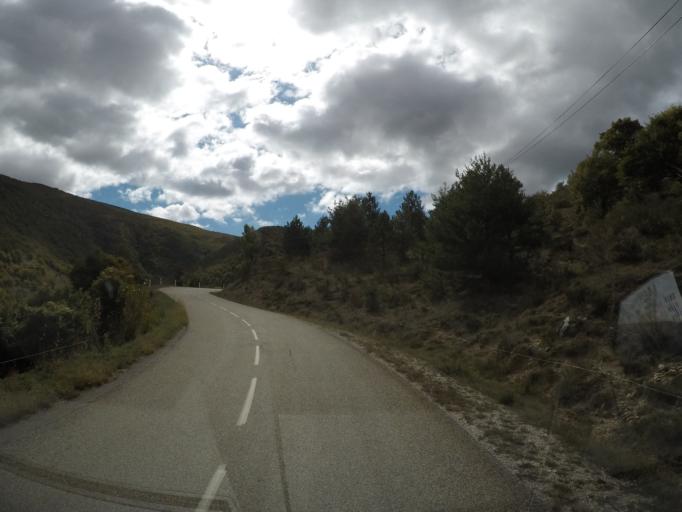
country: FR
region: Provence-Alpes-Cote d'Azur
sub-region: Departement du Vaucluse
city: Sault
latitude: 44.1850
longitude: 5.5315
